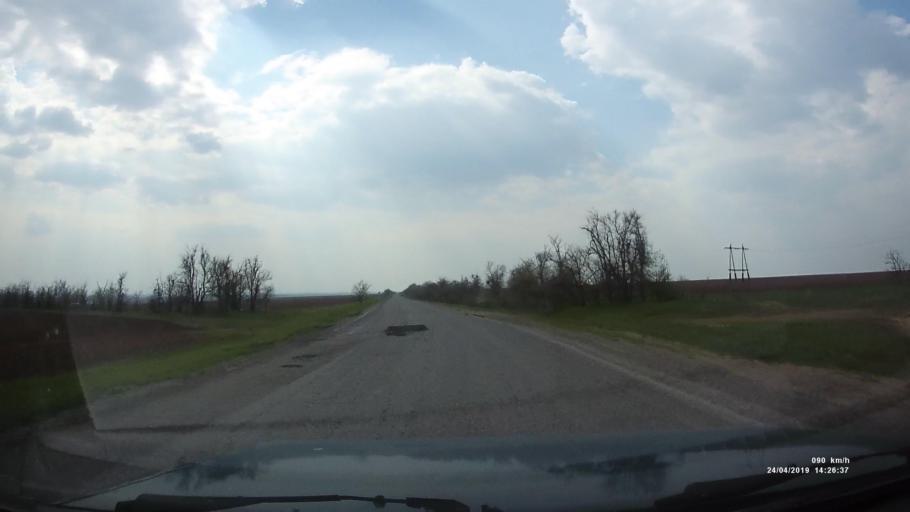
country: RU
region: Kalmykiya
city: Arshan'
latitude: 46.3344
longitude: 44.0591
